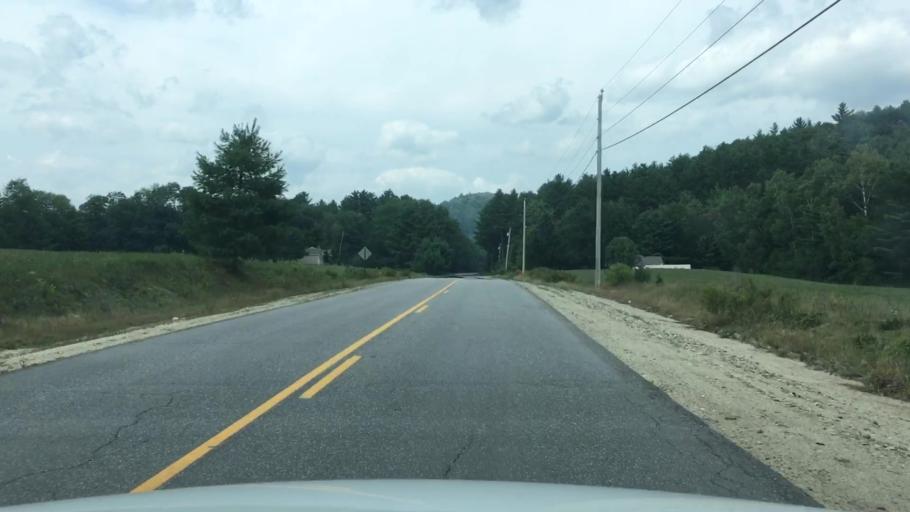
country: US
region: Maine
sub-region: Oxford County
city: Rumford
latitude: 44.5416
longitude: -70.6753
